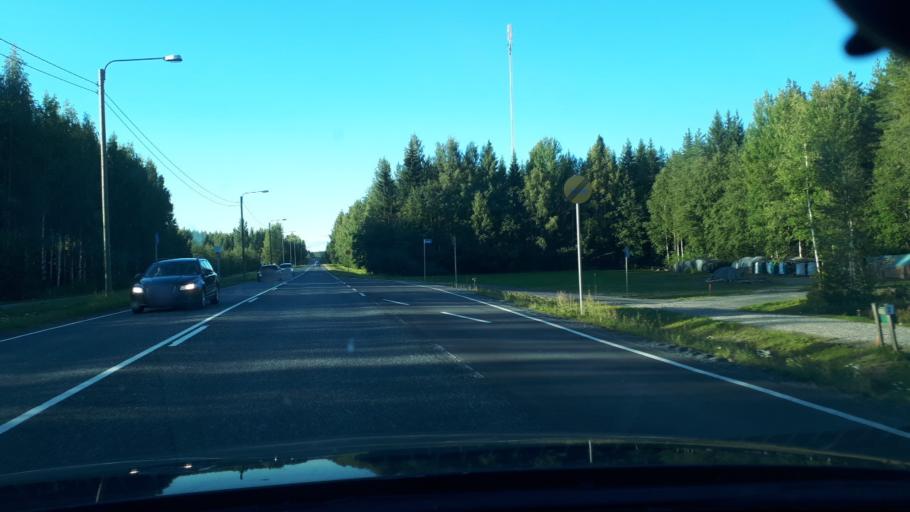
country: FI
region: Northern Savo
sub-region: Ylae-Savo
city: Lapinlahti
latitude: 63.4256
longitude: 27.3296
